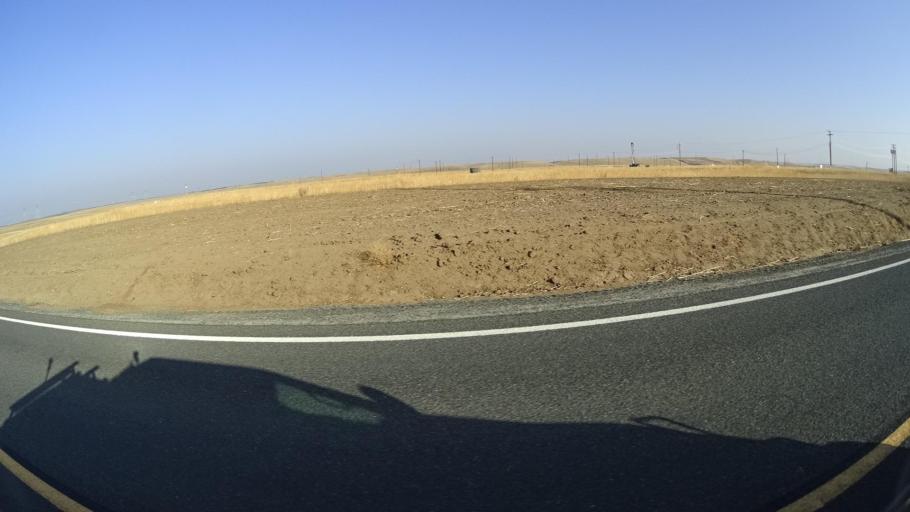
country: US
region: California
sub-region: Tulare County
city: Richgrove
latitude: 35.7619
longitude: -119.0597
